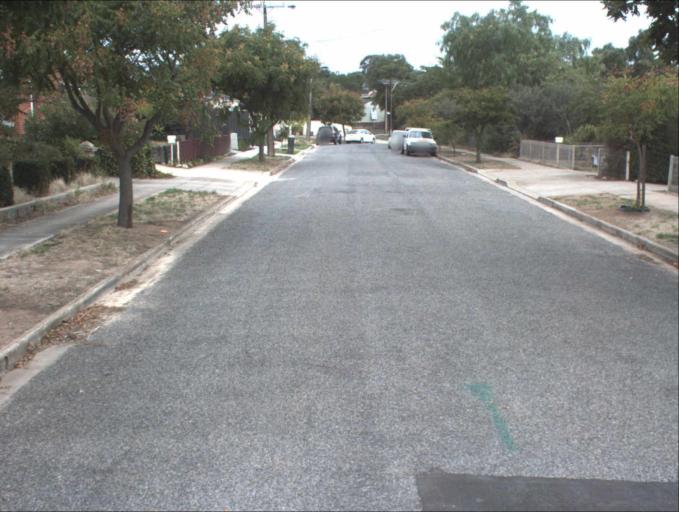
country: AU
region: South Australia
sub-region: Port Adelaide Enfield
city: Enfield
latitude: -34.8553
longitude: 138.6051
